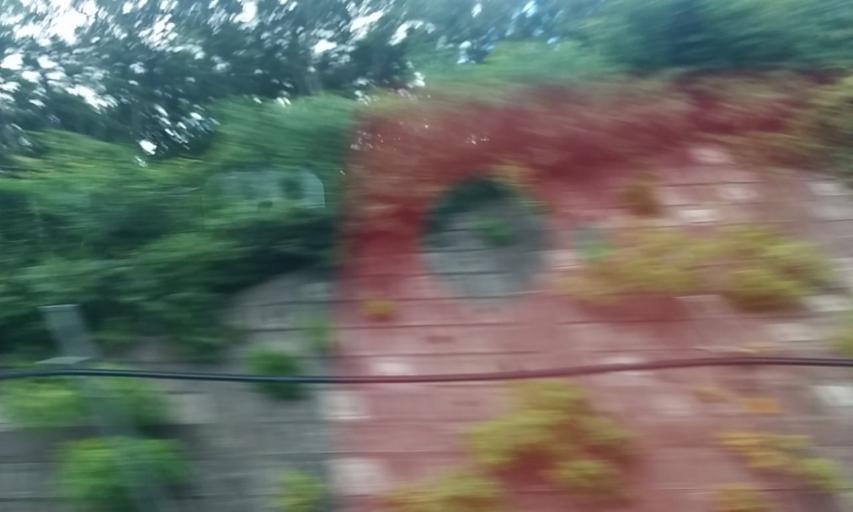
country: JP
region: Fukushima
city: Sukagawa
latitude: 37.3203
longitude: 140.3550
